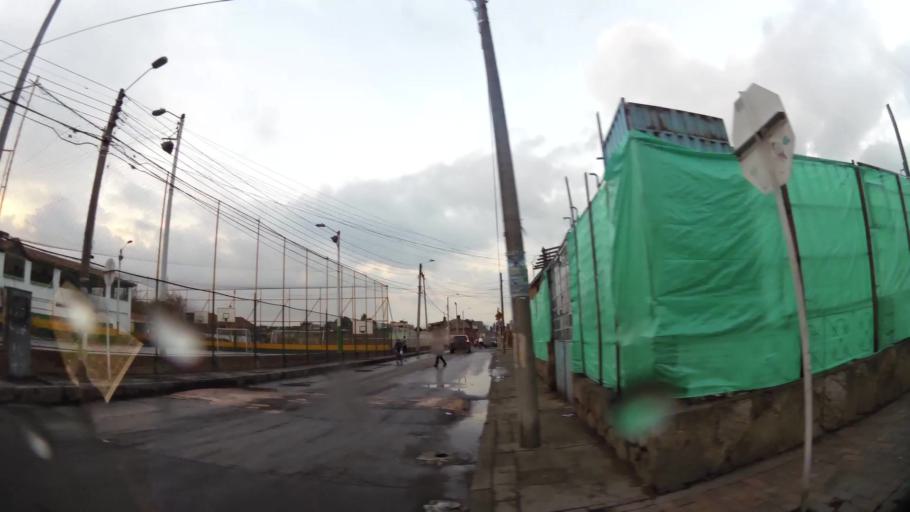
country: CO
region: Cundinamarca
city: Chia
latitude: 4.8555
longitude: -74.0557
